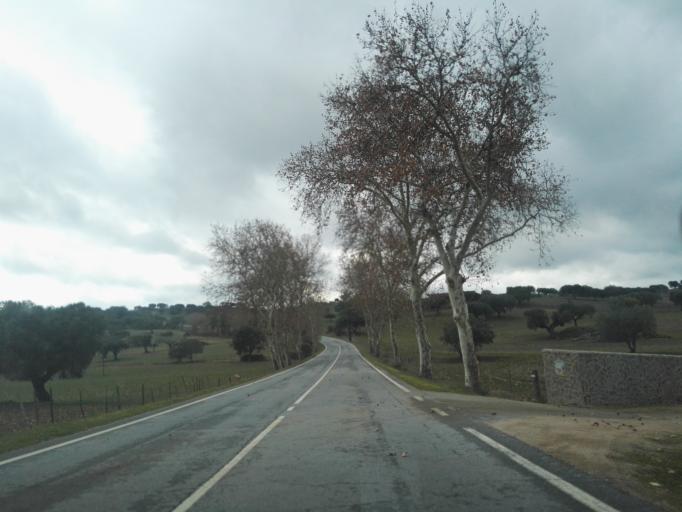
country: PT
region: Portalegre
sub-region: Arronches
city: Arronches
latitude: 39.0929
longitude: -7.2829
